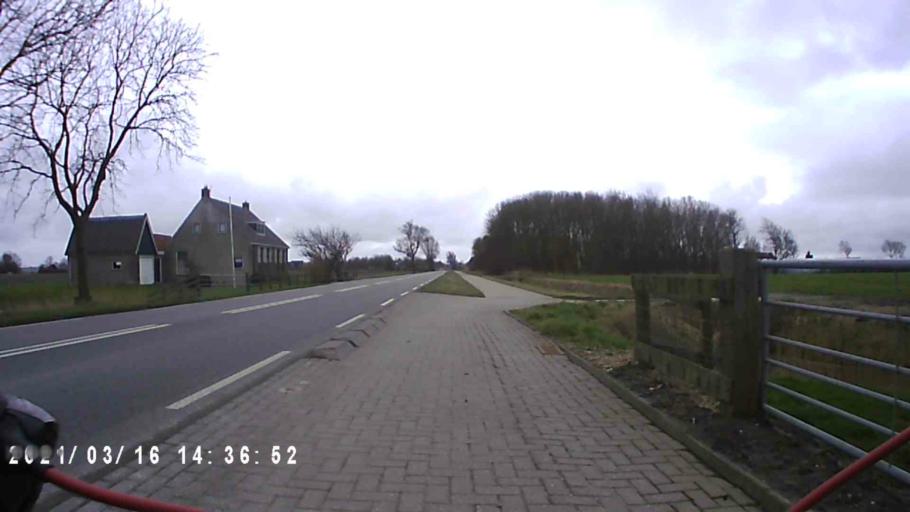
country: NL
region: Friesland
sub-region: Gemeente Harlingen
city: Harlingen
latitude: 53.1453
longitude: 5.4235
